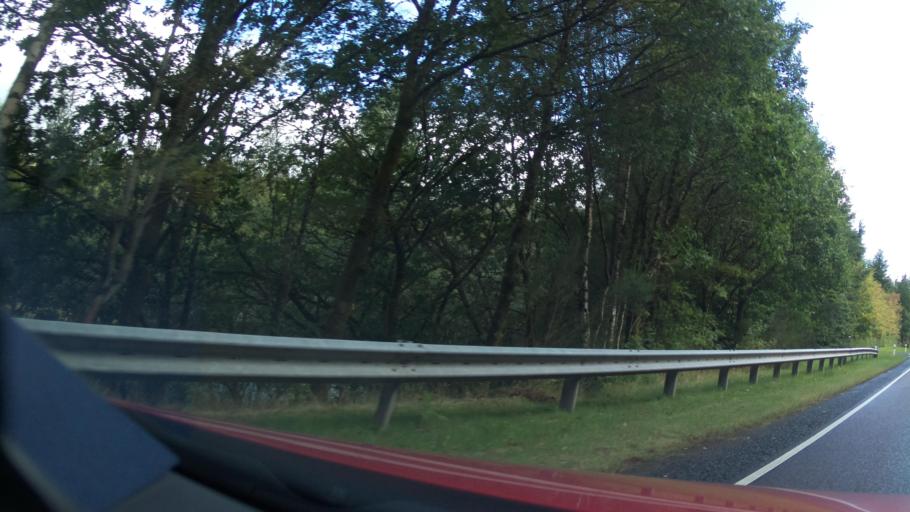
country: GB
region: Scotland
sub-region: Stirling
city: Callander
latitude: 56.4113
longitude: -4.5330
